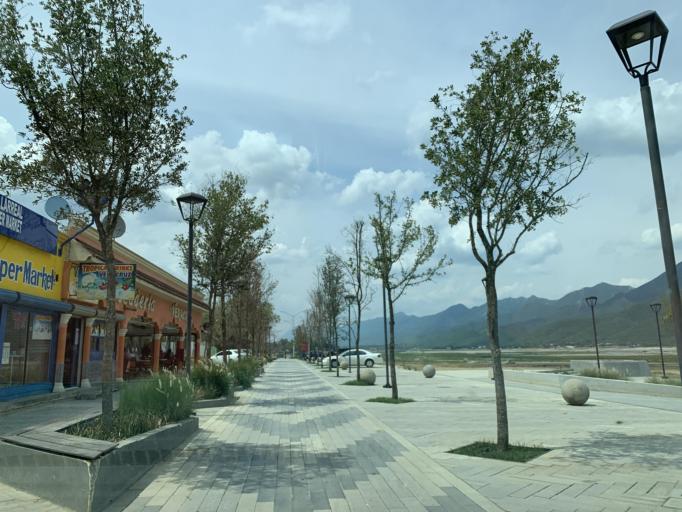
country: MX
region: Nuevo Leon
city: Santiago
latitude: 25.4140
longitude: -100.1393
